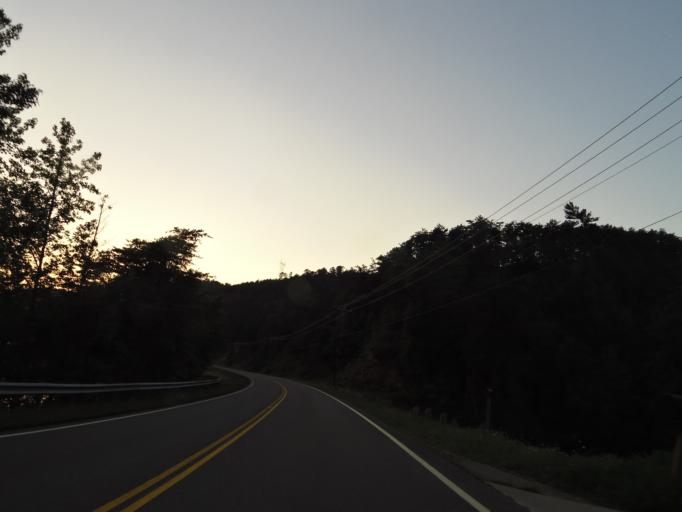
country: US
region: Tennessee
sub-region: Loudon County
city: Greenback
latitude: 35.5455
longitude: -84.0444
